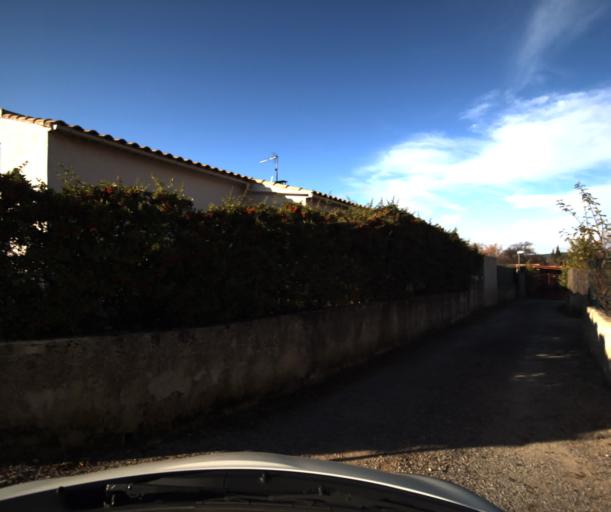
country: FR
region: Provence-Alpes-Cote d'Azur
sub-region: Departement du Vaucluse
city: Pertuis
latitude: 43.6955
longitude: 5.5216
